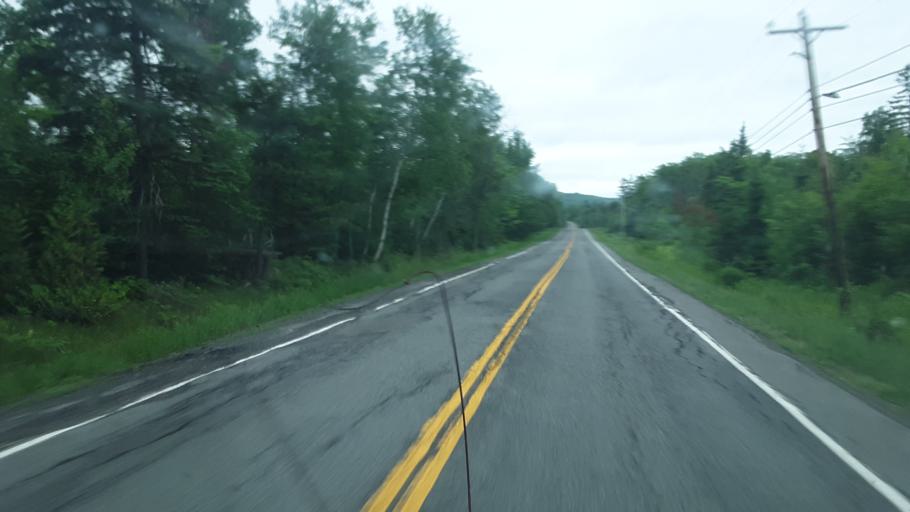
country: US
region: Maine
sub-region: Penobscot County
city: Patten
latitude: 46.1072
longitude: -68.4150
